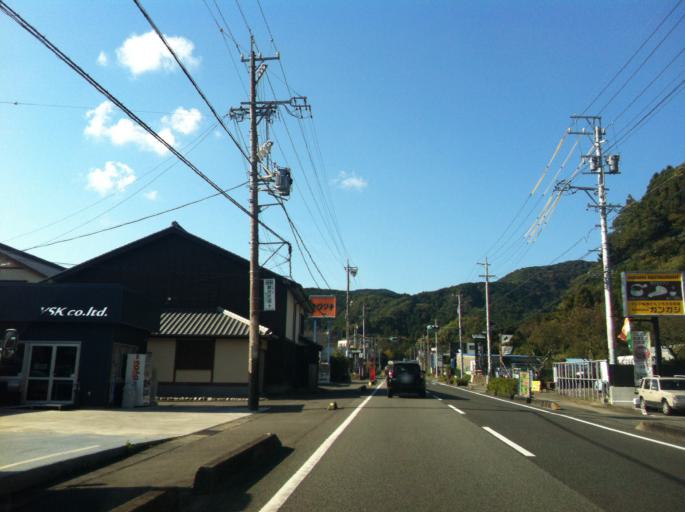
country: JP
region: Shizuoka
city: Shizuoka-shi
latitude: 34.9506
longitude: 138.3394
